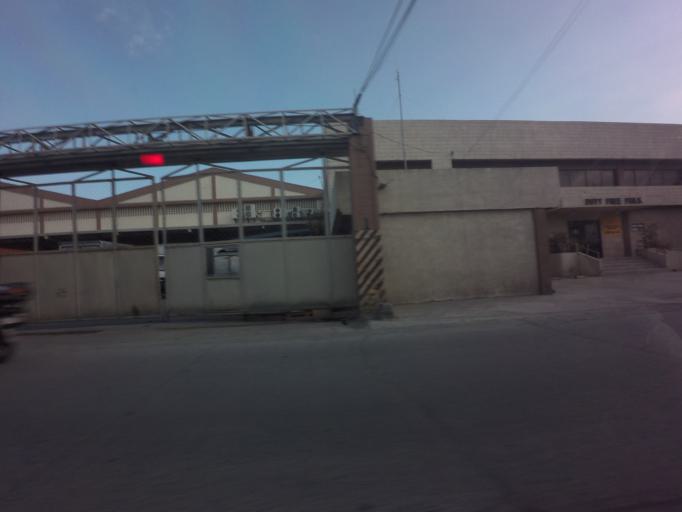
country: PH
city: Sambayanihan People's Village
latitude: 14.4975
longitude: 121.0027
